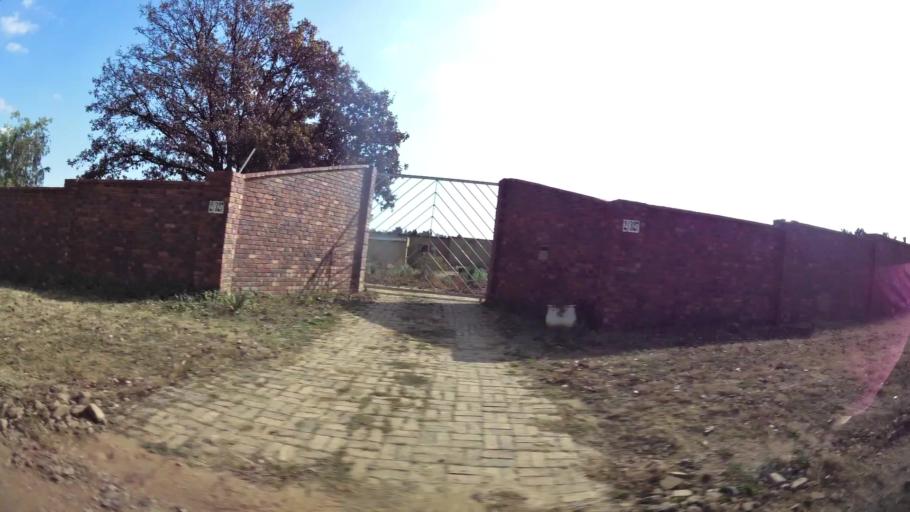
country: ZA
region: Gauteng
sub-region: Ekurhuleni Metropolitan Municipality
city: Benoni
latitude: -26.0934
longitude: 28.3549
